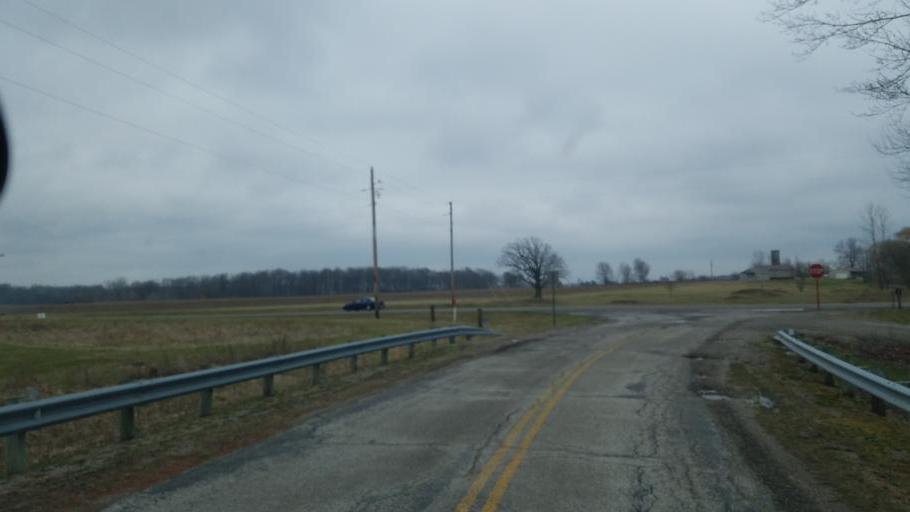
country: US
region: Ohio
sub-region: Morrow County
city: Mount Gilead
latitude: 40.6530
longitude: -82.8909
